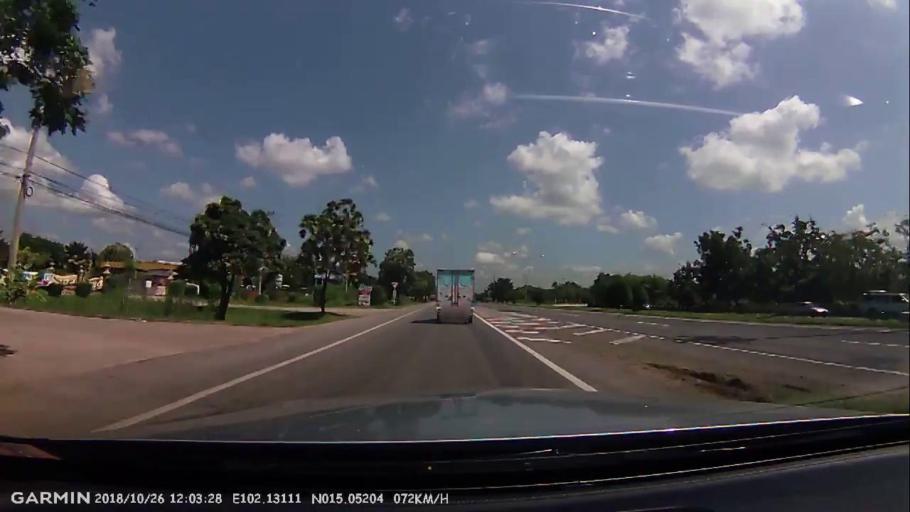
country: TH
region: Nakhon Ratchasima
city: Nakhon Ratchasima
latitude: 15.0521
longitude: 102.1313
